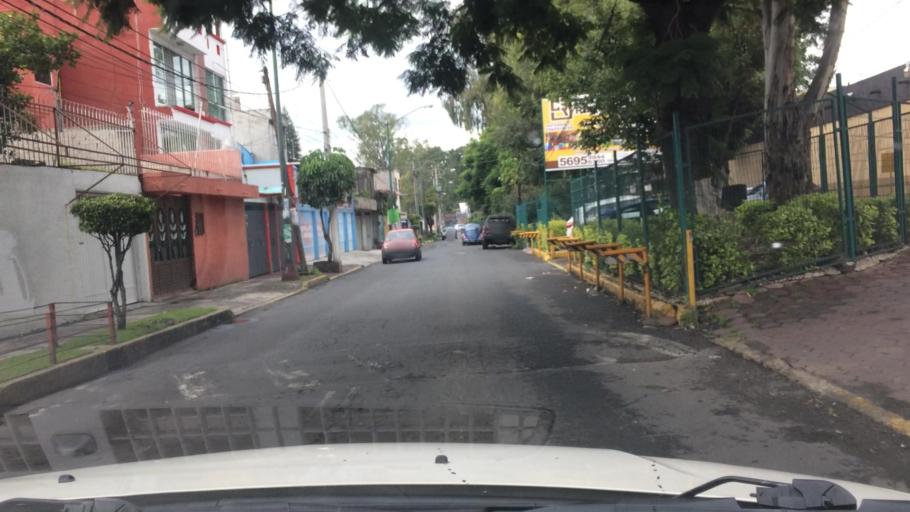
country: MX
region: Mexico City
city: Iztapalapa
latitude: 19.3221
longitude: -99.0982
